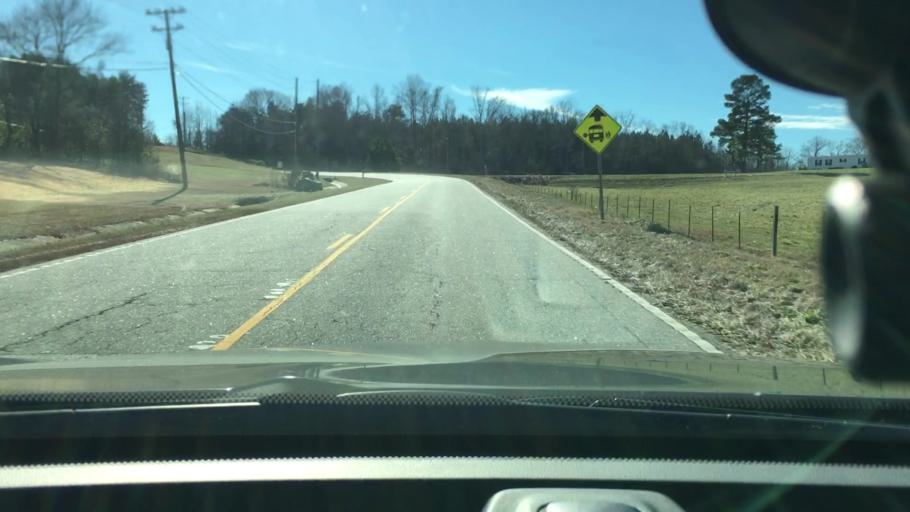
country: US
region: South Carolina
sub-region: Cherokee County
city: Gaffney
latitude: 35.0210
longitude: -81.6897
